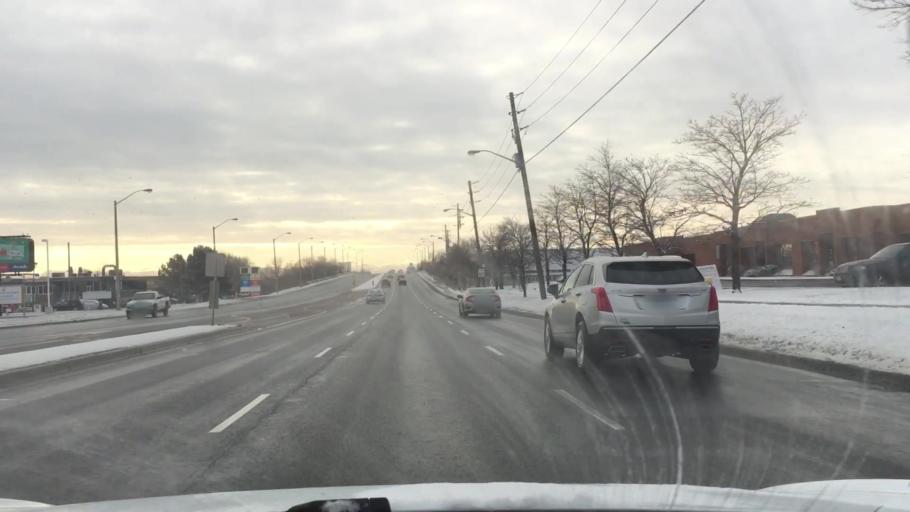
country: CA
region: Ontario
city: Scarborough
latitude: 43.8200
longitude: -79.2462
